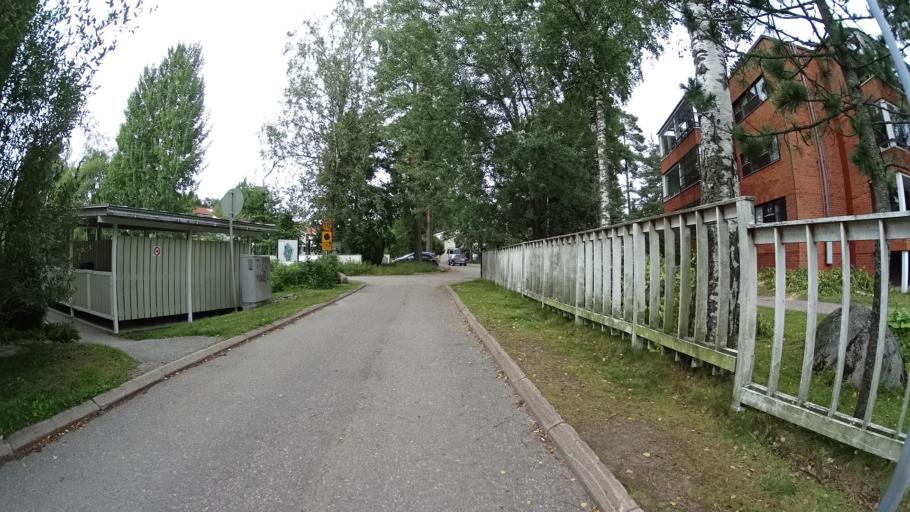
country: FI
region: Uusimaa
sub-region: Helsinki
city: Kilo
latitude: 60.1880
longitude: 24.7874
